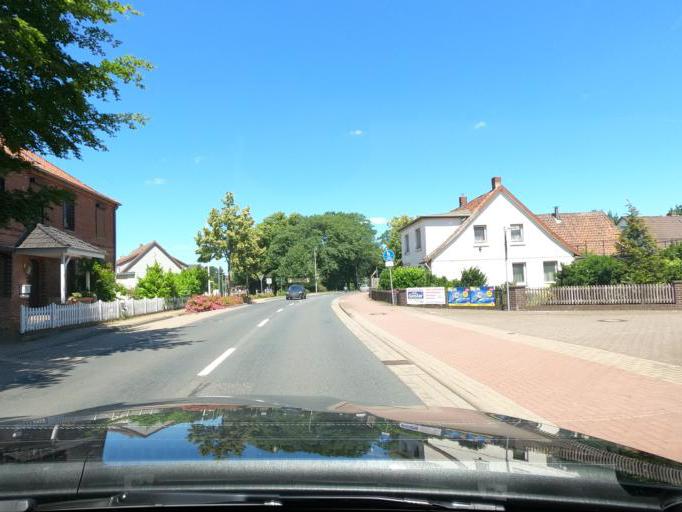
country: DE
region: Lower Saxony
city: Lehrte
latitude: 52.3993
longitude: 9.9740
